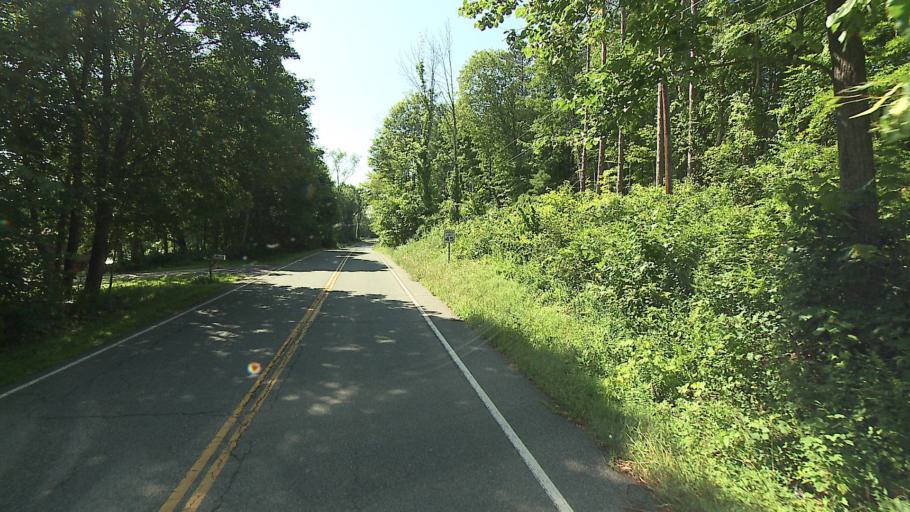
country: US
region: Massachusetts
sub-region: Berkshire County
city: Sheffield
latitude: 42.0475
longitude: -73.4251
